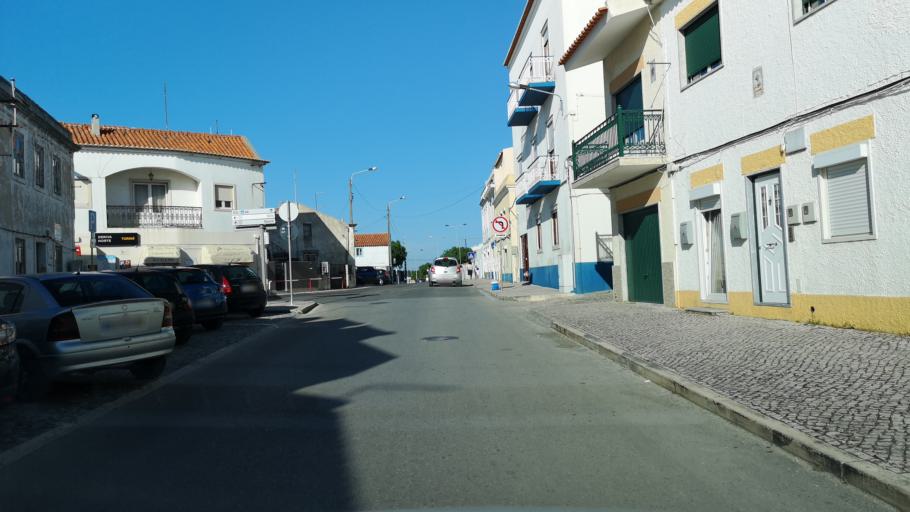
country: PT
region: Leiria
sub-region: Nazare
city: Nazare
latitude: 39.6058
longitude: -9.0726
